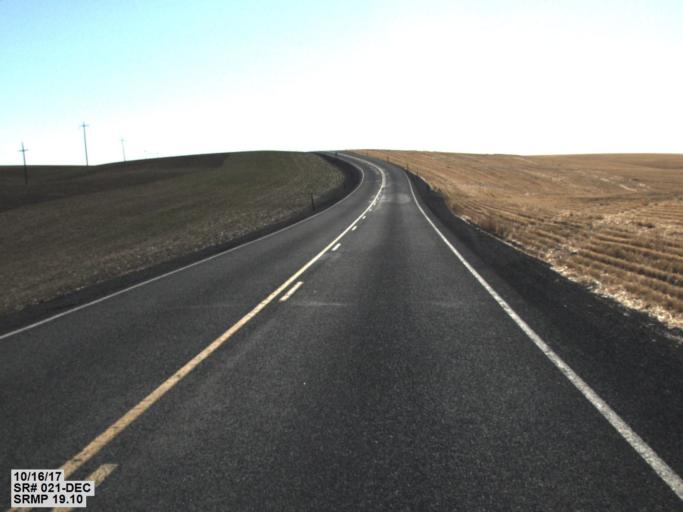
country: US
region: Washington
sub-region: Adams County
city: Ritzville
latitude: 46.8968
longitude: -118.5685
